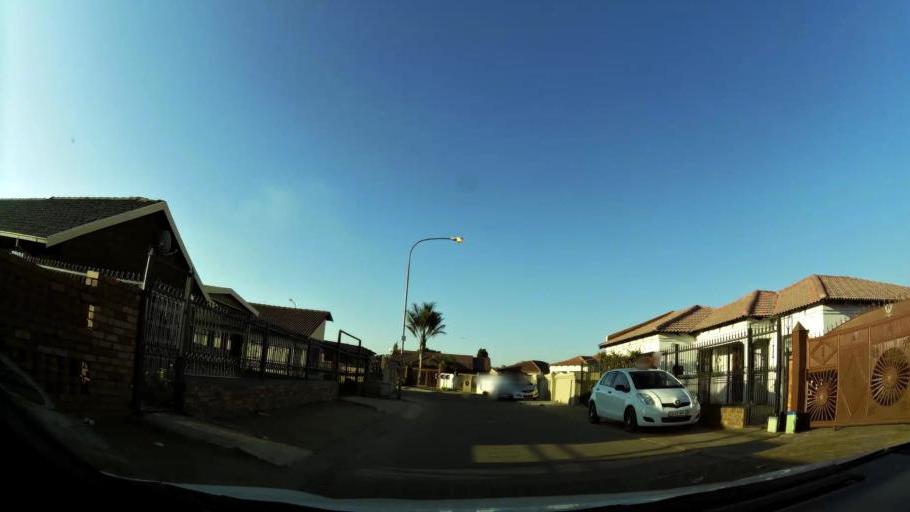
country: ZA
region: Gauteng
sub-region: City of Tshwane Metropolitan Municipality
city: Cullinan
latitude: -25.7245
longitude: 28.3952
